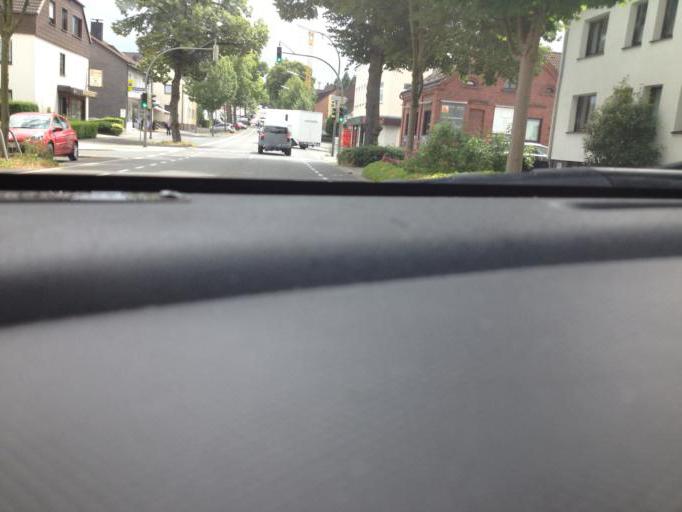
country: DE
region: North Rhine-Westphalia
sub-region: Regierungsbezirk Arnsberg
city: Dortmund
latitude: 51.4592
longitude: 7.4560
